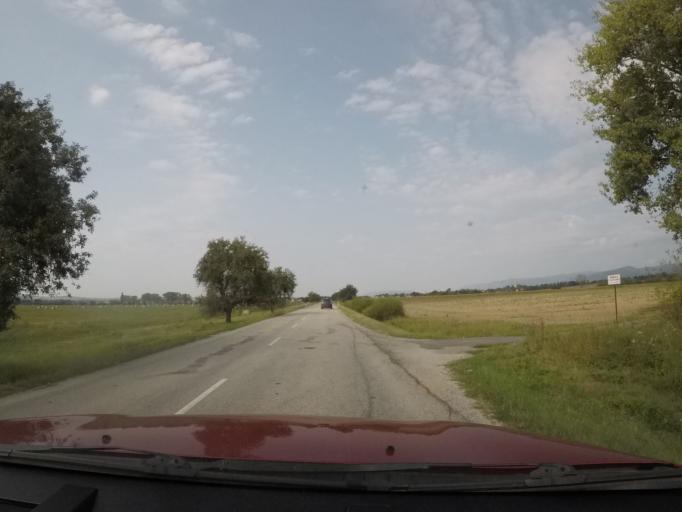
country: SK
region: Kosicky
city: Moldava nad Bodvou
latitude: 48.5964
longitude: 21.0373
